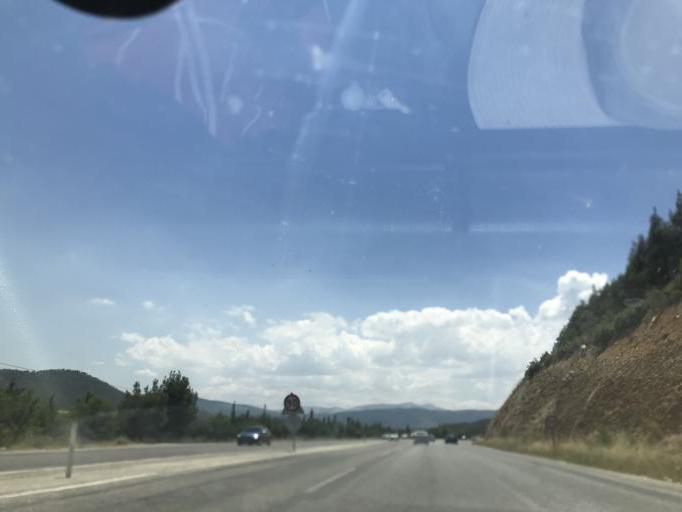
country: TR
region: Denizli
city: Honaz
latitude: 37.7184
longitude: 29.2082
